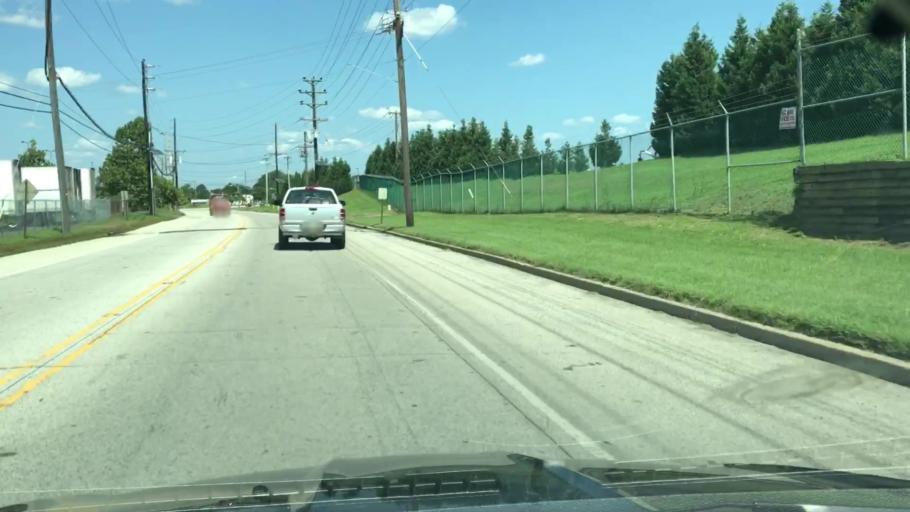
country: US
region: New Jersey
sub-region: Burlington County
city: Palmyra
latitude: 39.9905
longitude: -75.0399
